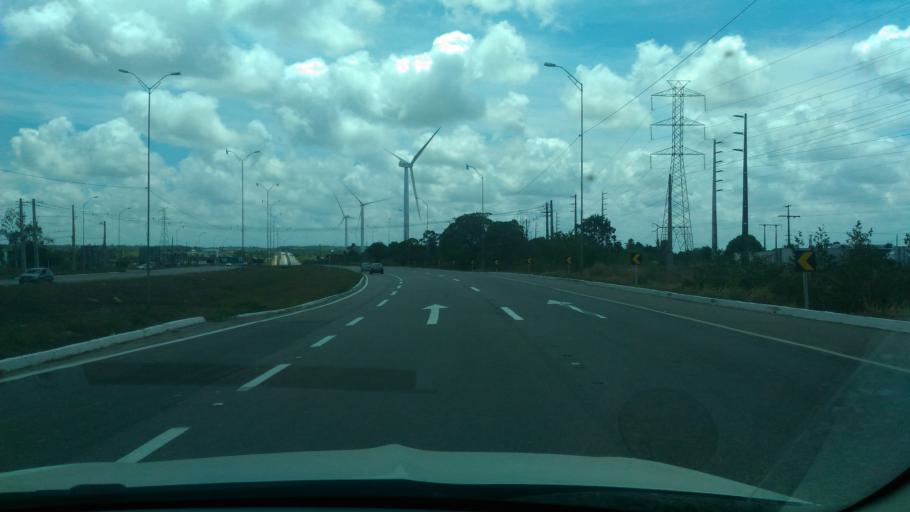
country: BR
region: Paraiba
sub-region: Conde
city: Conde
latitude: -7.2578
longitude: -34.9355
